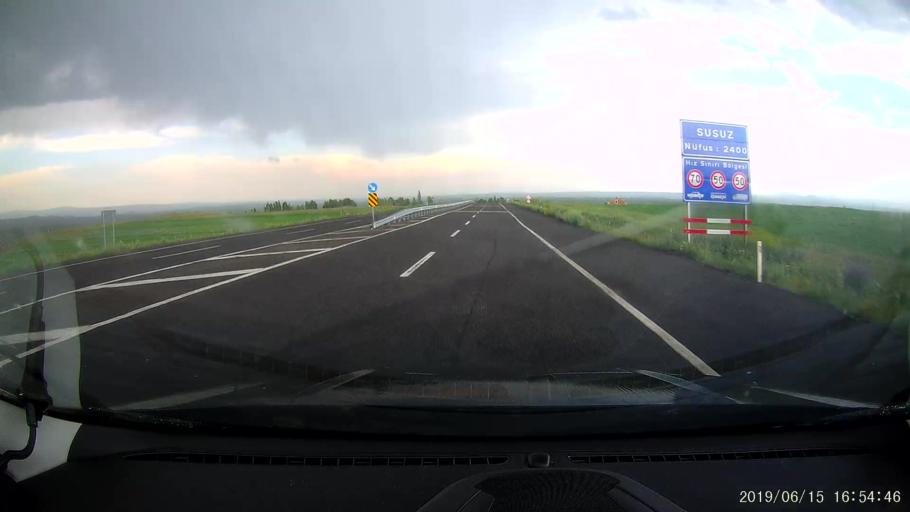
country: TR
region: Kars
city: Susuz
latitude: 40.7887
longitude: 43.1313
